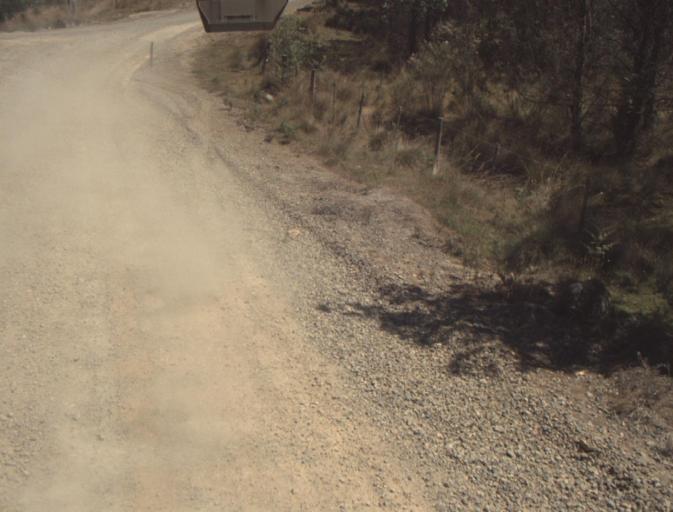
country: AU
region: Tasmania
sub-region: Dorset
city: Scottsdale
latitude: -41.3199
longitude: 147.4592
